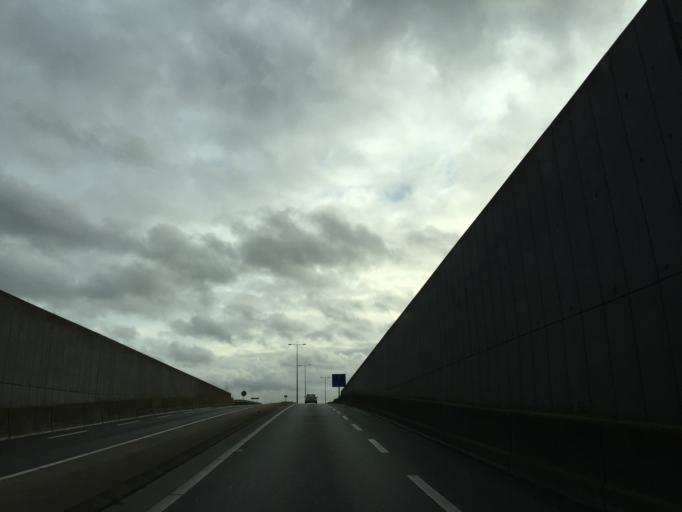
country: NL
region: South Holland
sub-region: Gemeente Lansingerland
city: Berkel en Rodenrijs
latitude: 52.0059
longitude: 4.4551
